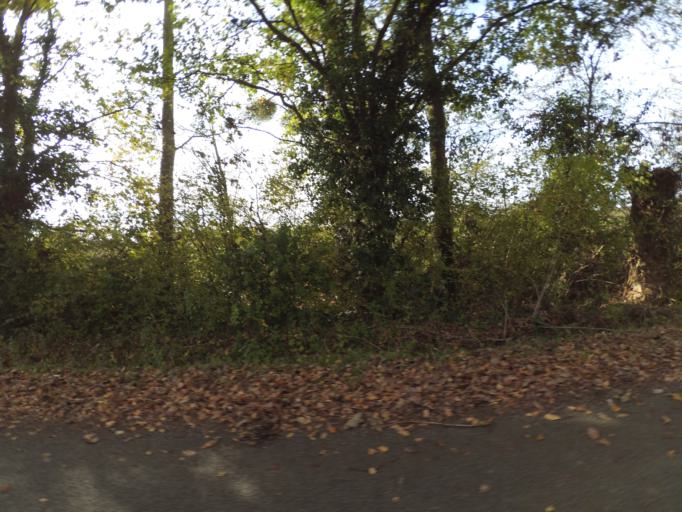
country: FR
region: Pays de la Loire
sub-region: Departement de la Loire-Atlantique
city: Saint-Hilaire-de-Clisson
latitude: 47.0391
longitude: -1.3371
